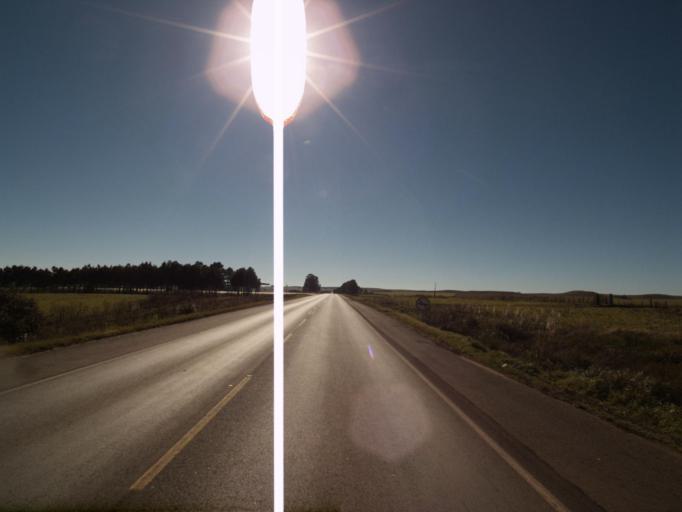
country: BR
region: Parana
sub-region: Palmas
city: Palmas
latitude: -26.7807
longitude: -51.6861
